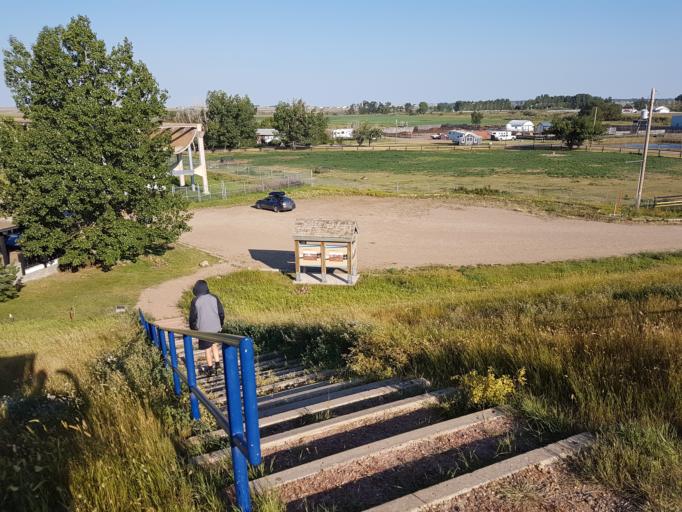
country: CA
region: Alberta
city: Brooks
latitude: 50.5318
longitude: -111.8375
